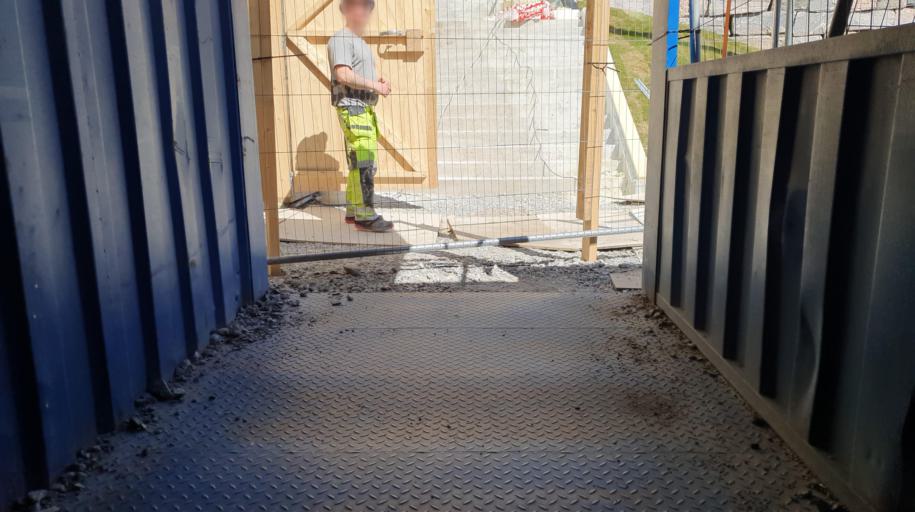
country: NO
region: More og Romsdal
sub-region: Sula
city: Langevag
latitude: 62.4715
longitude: 6.2344
